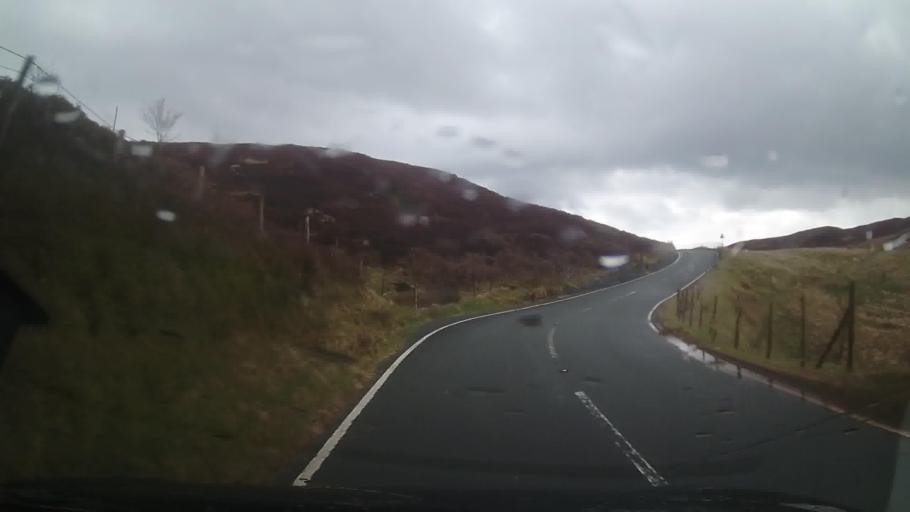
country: GB
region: Wales
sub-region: Gwynedd
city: Ffestiniog
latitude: 52.9586
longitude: -3.8786
